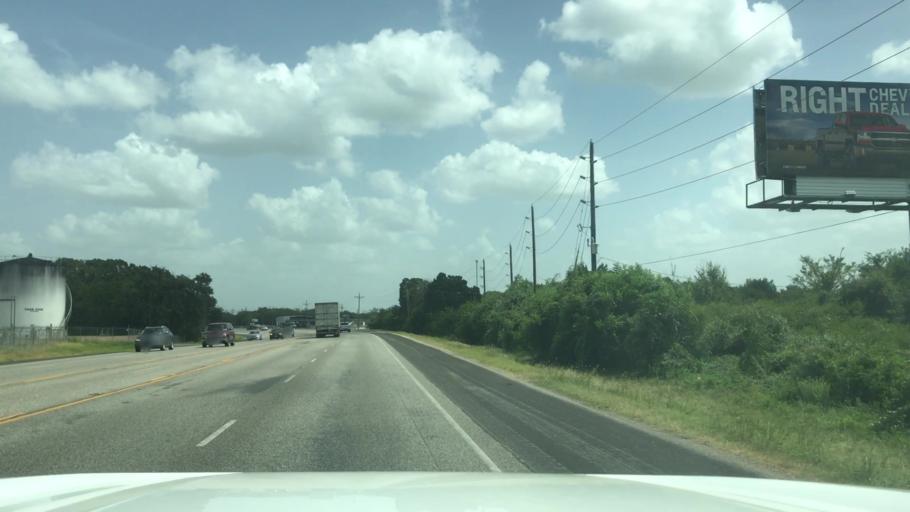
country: US
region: Texas
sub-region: Robertson County
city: Hearne
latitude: 30.8621
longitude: -96.5808
